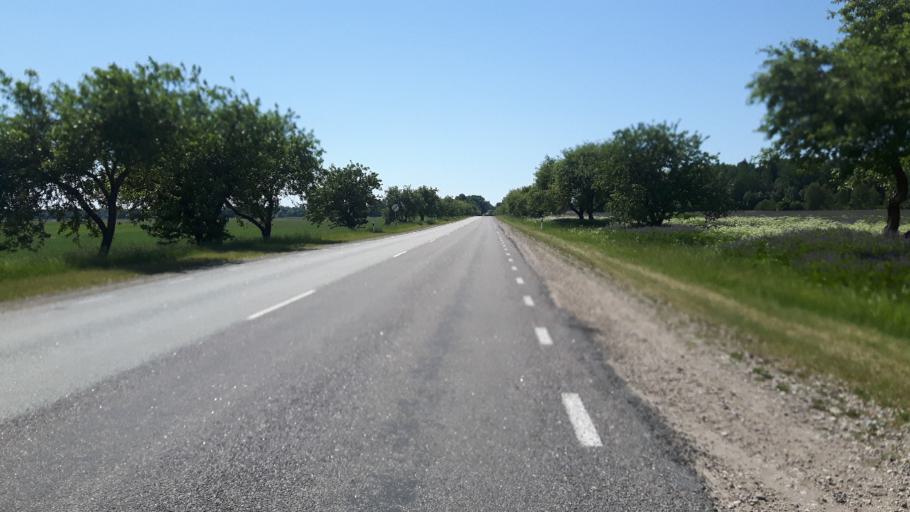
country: EE
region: Paernumaa
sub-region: Tootsi vald
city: Tootsi
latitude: 58.4739
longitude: 24.8010
